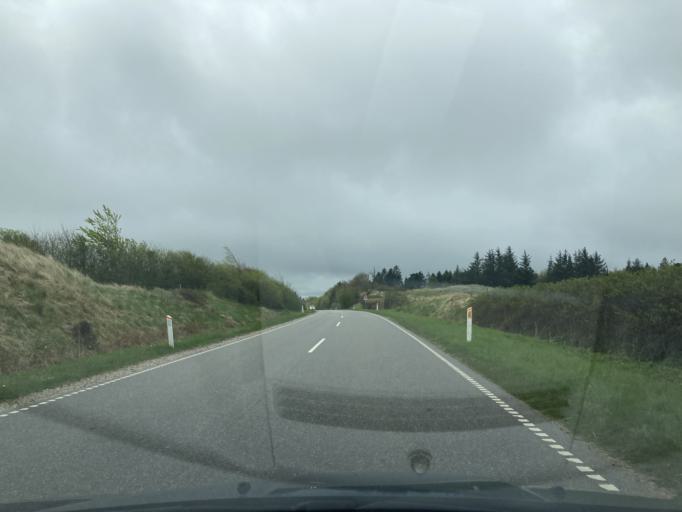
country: DK
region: North Denmark
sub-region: Thisted Kommune
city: Hurup
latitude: 56.8792
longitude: 8.3863
